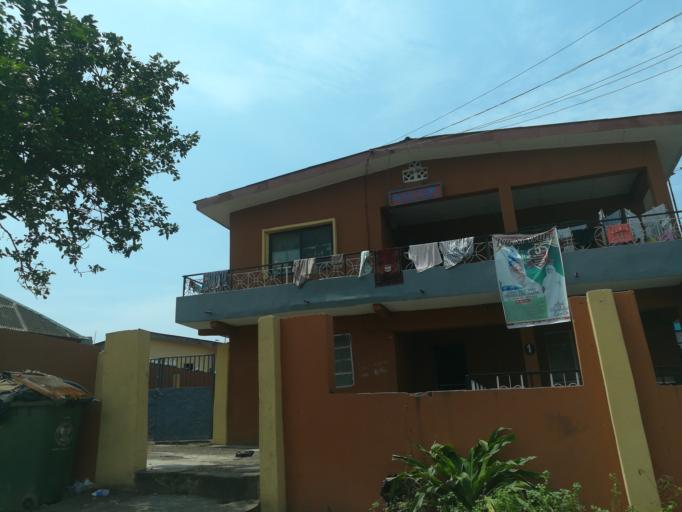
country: NG
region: Lagos
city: Ikorodu
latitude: 6.6211
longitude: 3.4963
